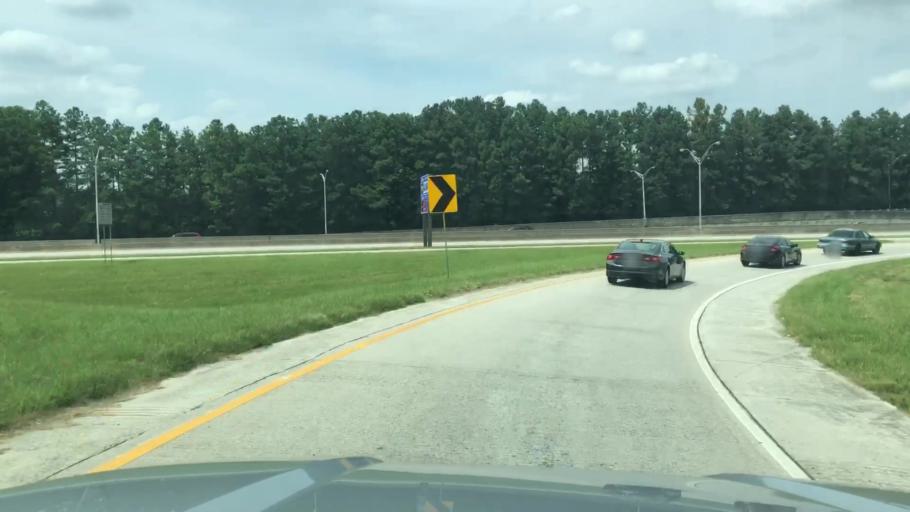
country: US
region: Georgia
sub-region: Fulton County
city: College Park
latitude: 33.6430
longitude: -84.4507
